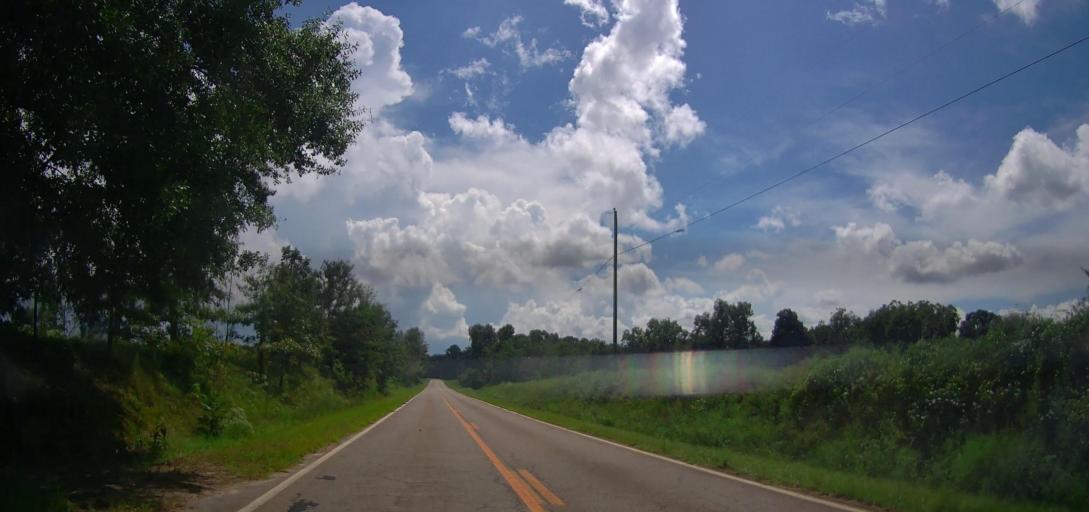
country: US
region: Georgia
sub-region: Peach County
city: Fort Valley
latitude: 32.5292
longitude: -83.8027
